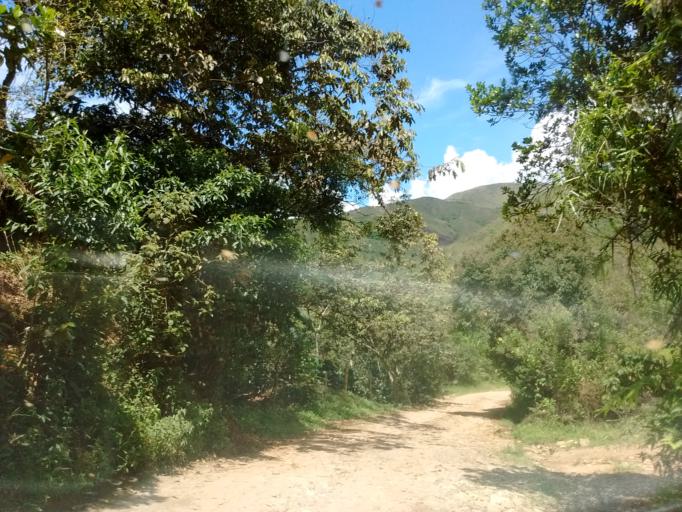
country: CO
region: Cauca
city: Villa Rica
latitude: 2.6459
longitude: -76.7704
